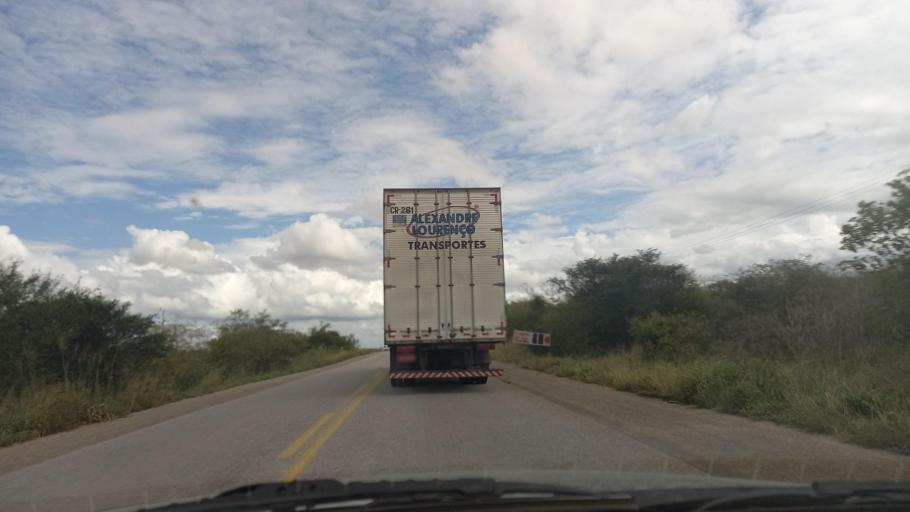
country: BR
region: Pernambuco
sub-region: Cachoeirinha
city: Cachoeirinha
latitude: -8.3881
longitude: -36.1768
